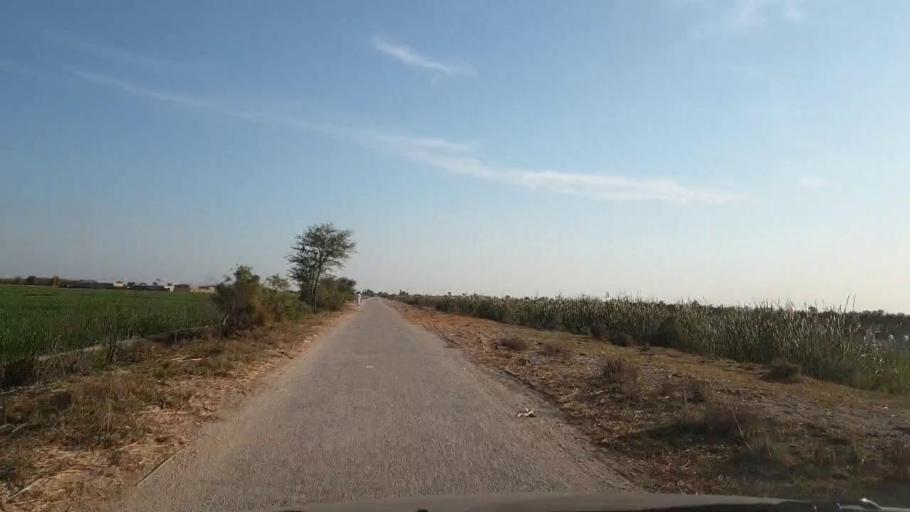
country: PK
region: Sindh
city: Khadro
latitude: 26.2101
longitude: 68.7450
